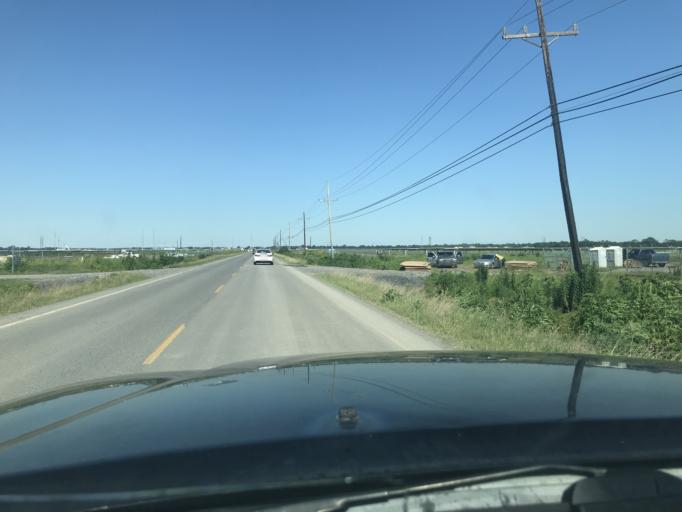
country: US
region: Louisiana
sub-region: West Baton Rouge Parish
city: Brusly
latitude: 30.4688
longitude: -91.3221
